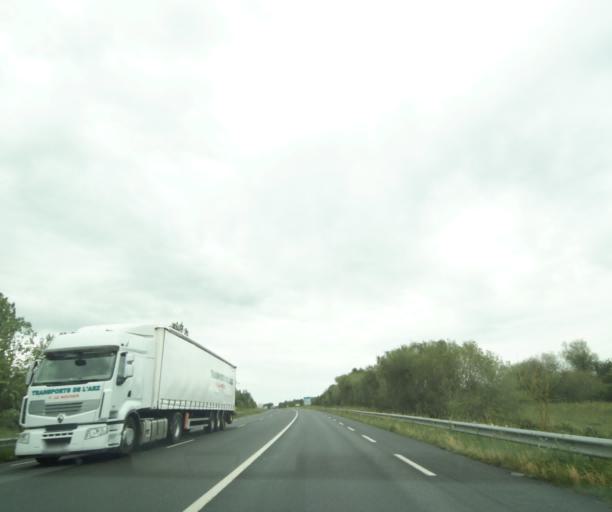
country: FR
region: Poitou-Charentes
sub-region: Departement des Deux-Sevres
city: Viennay
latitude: 46.7707
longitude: -0.2189
